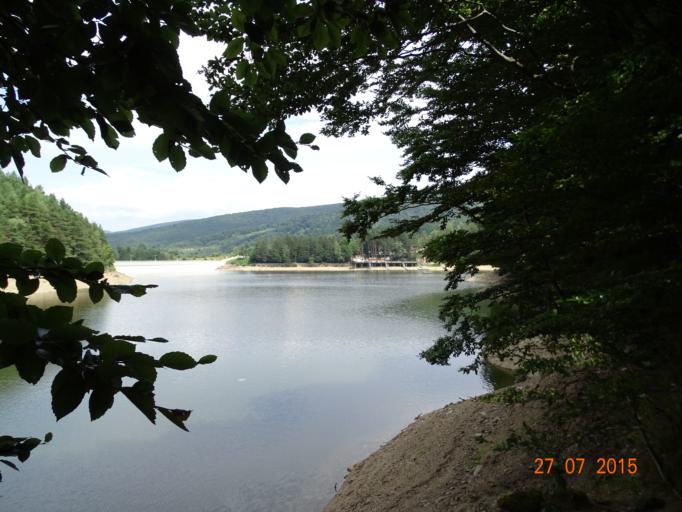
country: RO
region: Caras-Severin
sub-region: Comuna Valiug
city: Valiug
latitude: 45.2163
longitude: 22.0208
